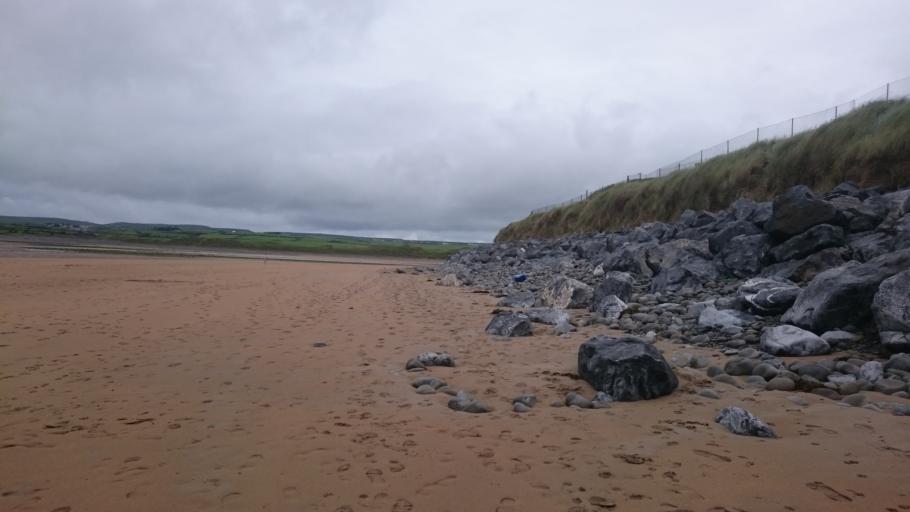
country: IE
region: Munster
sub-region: An Clar
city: Kilrush
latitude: 52.9403
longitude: -9.3575
